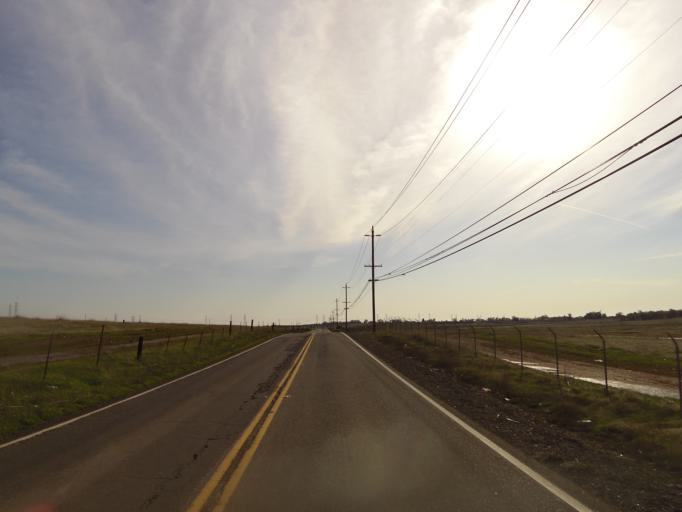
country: US
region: California
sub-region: Sacramento County
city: Folsom
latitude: 38.6204
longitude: -121.1505
